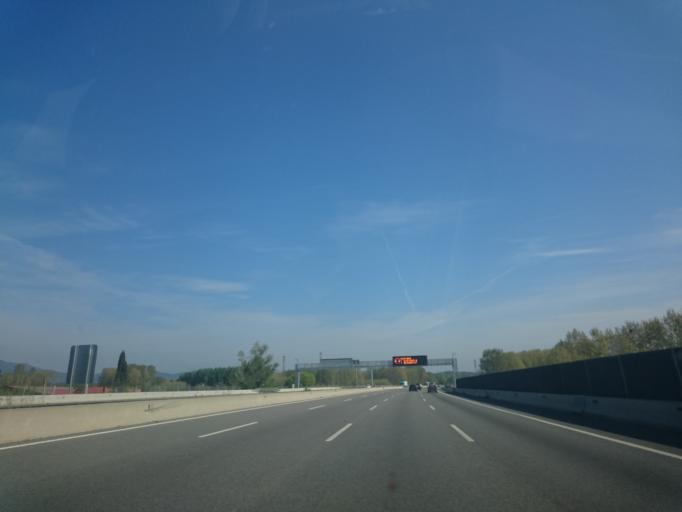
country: ES
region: Catalonia
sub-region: Provincia de Girona
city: Salt
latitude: 41.9747
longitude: 2.7786
